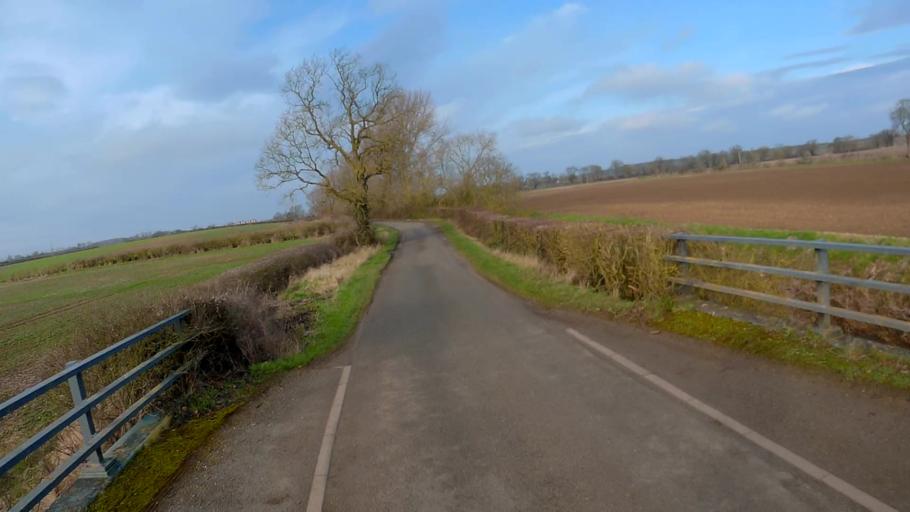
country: GB
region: England
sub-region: Lincolnshire
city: Bourne
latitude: 52.7709
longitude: -0.4243
